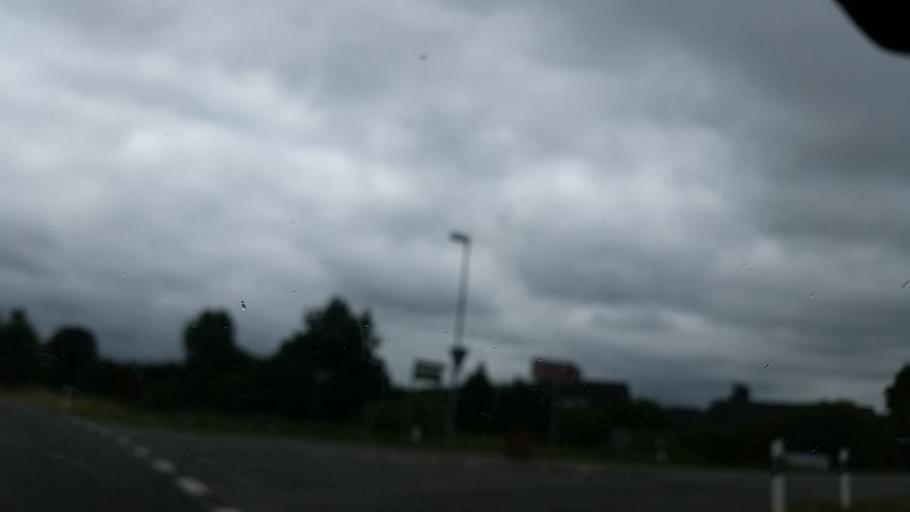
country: DE
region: Schleswig-Holstein
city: Dannewerk
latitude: 54.4856
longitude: 9.5083
